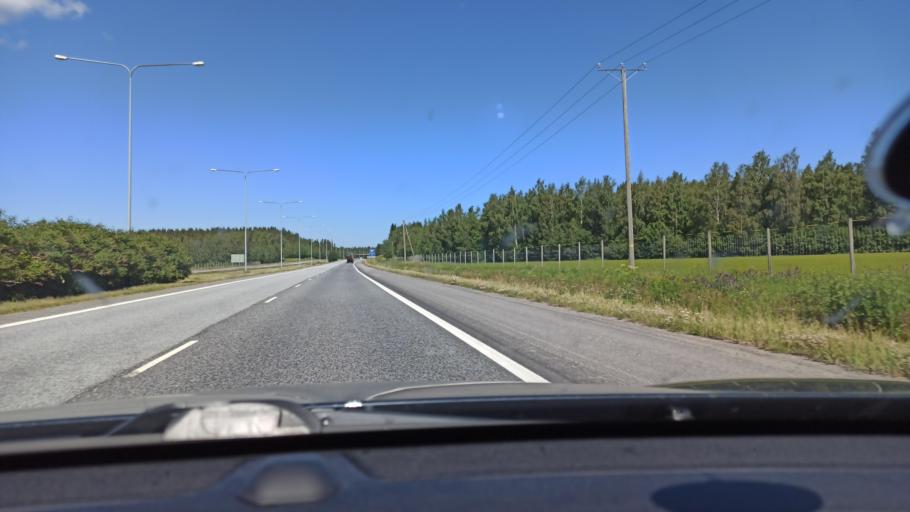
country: FI
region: Ostrobothnia
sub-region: Vaasa
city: Ristinummi
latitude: 63.0462
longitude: 21.7232
